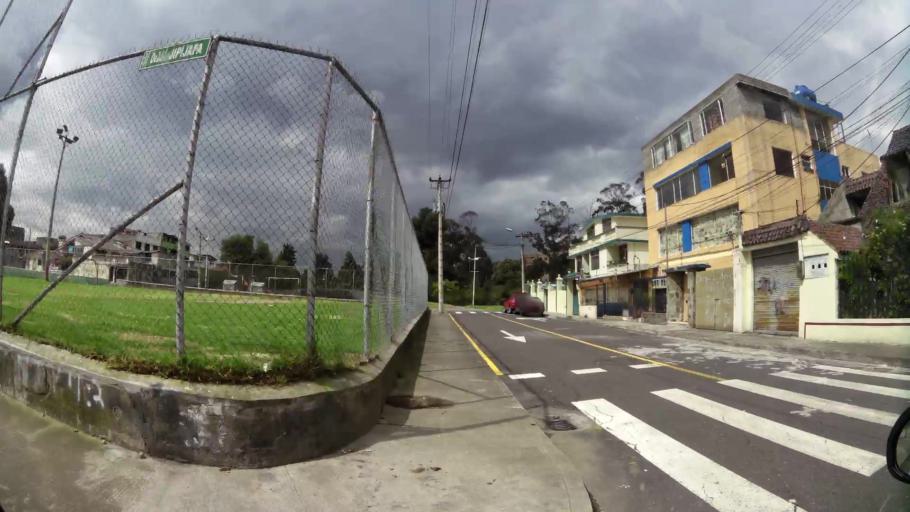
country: EC
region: Pichincha
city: Quito
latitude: -0.2521
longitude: -78.5270
